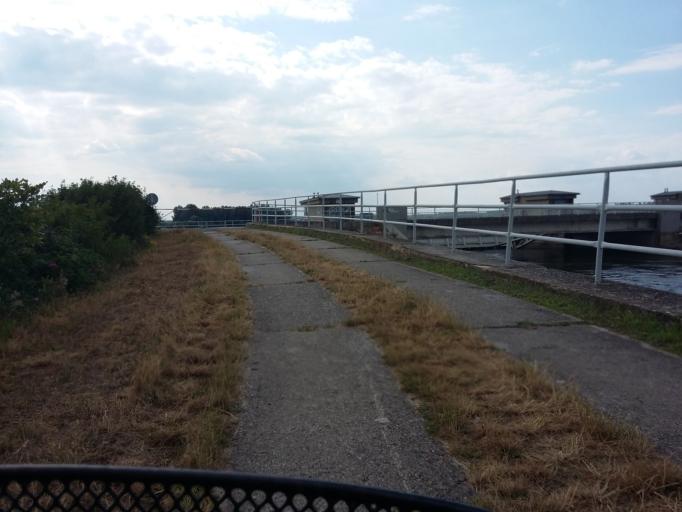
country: CZ
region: South Moravian
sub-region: Okres Breclav
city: Dolni Dunajovice
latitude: 48.8927
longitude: 16.6449
